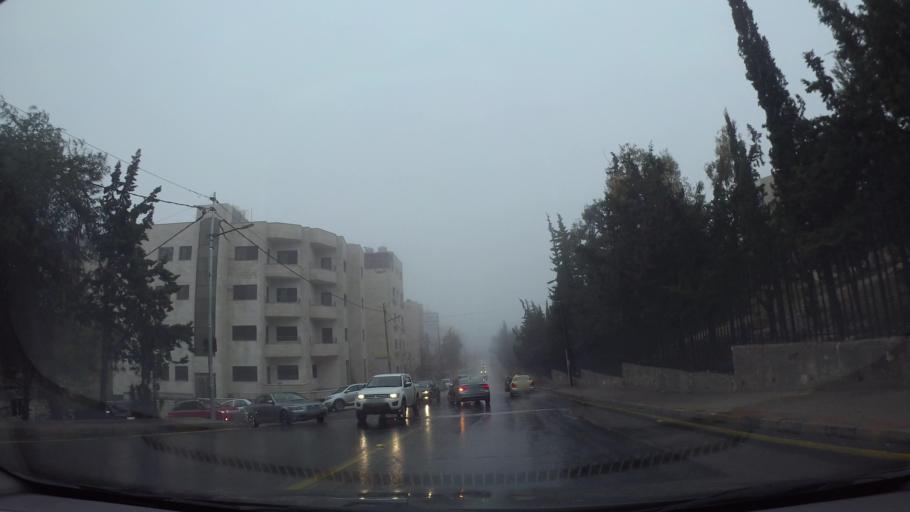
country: JO
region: Amman
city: Al Jubayhah
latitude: 32.0211
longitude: 35.8762
